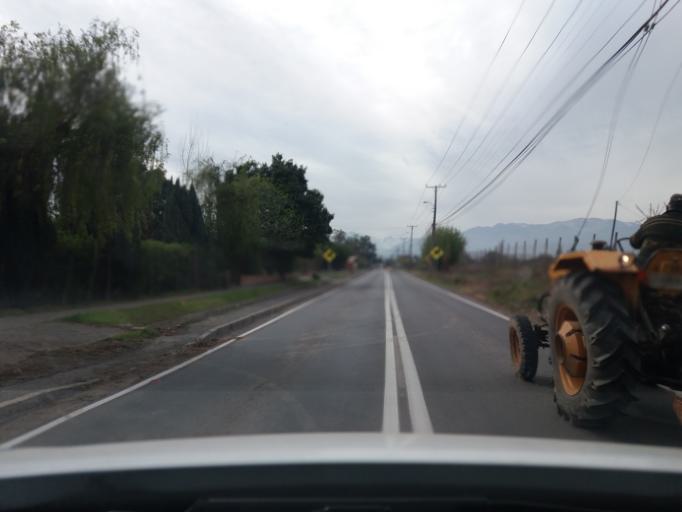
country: CL
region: Valparaiso
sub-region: Provincia de Los Andes
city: Los Andes
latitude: -32.8246
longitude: -70.6612
